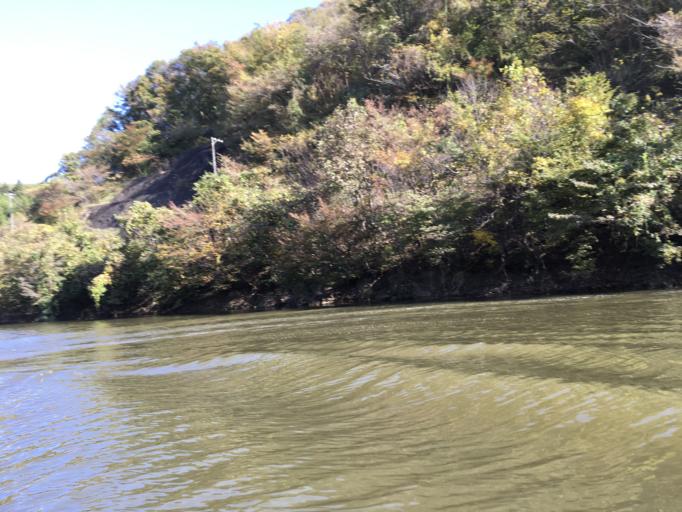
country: JP
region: Iwate
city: Ichinoseki
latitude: 38.8010
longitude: 141.2900
